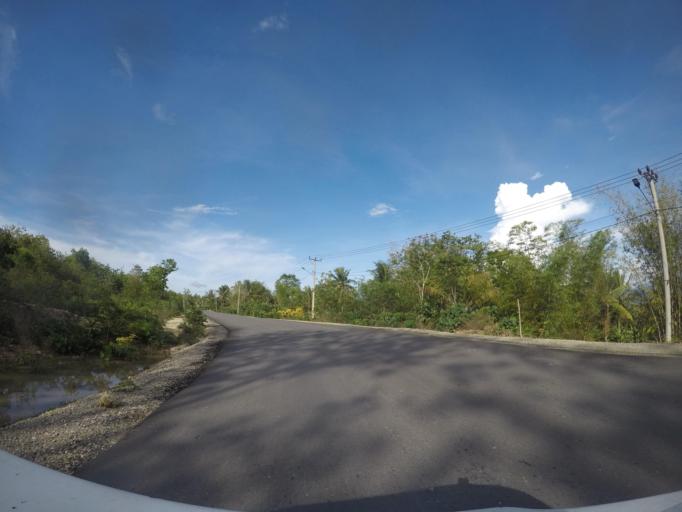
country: TL
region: Baucau
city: Baucau
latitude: -8.4959
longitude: 126.4545
